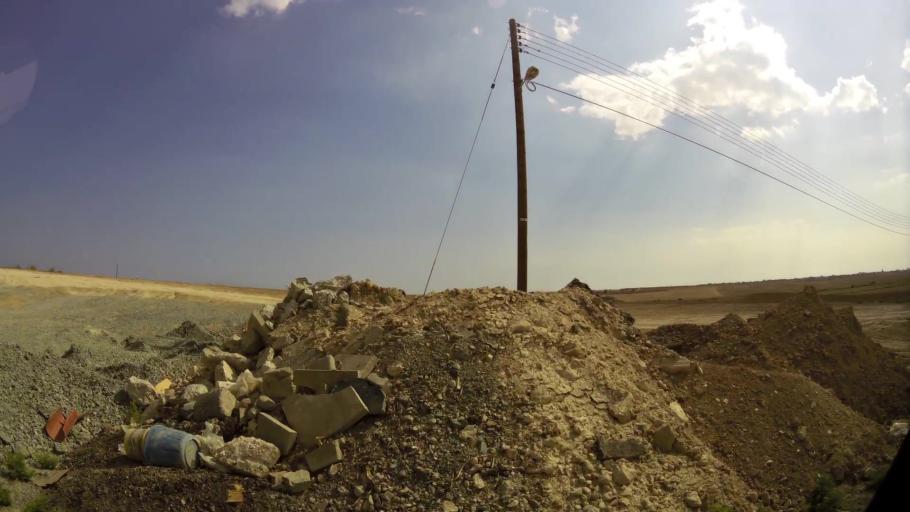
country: CY
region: Larnaka
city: Larnaca
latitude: 34.9067
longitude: 33.5974
